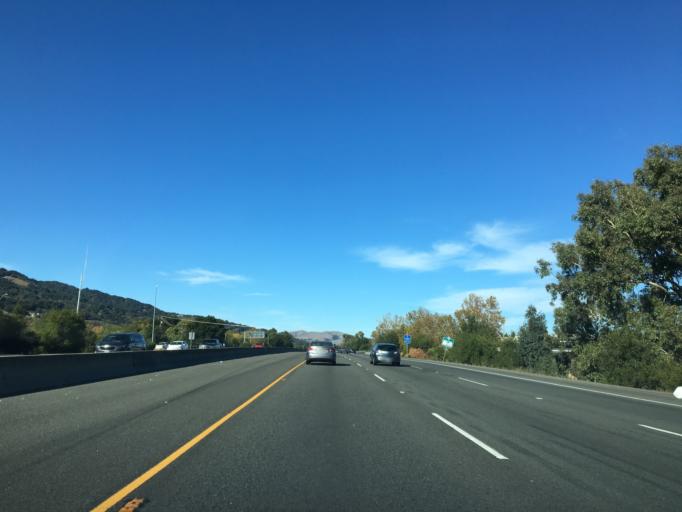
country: US
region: California
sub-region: Alameda County
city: Pleasanton
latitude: 37.6554
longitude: -121.9000
